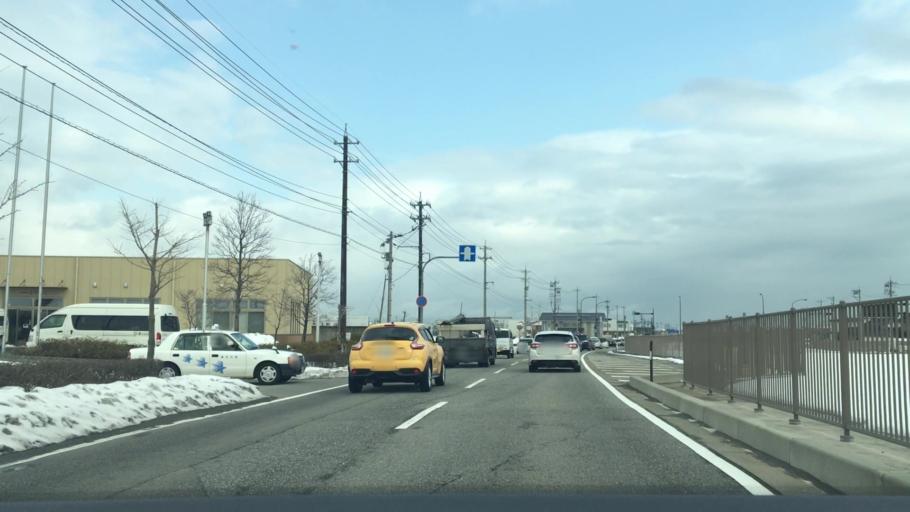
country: JP
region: Ishikawa
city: Matsuto
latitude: 36.5583
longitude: 136.5792
